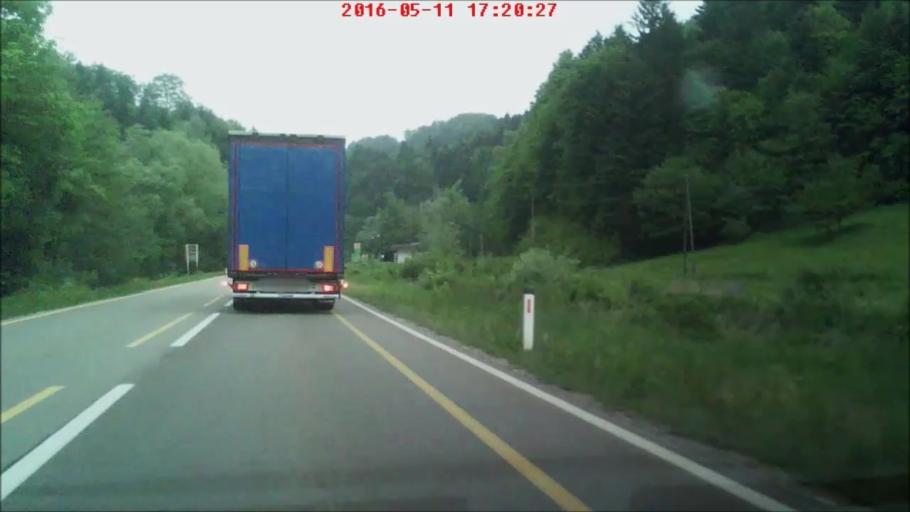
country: SI
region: Zetale
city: Zetale
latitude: 46.2918
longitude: 15.8565
